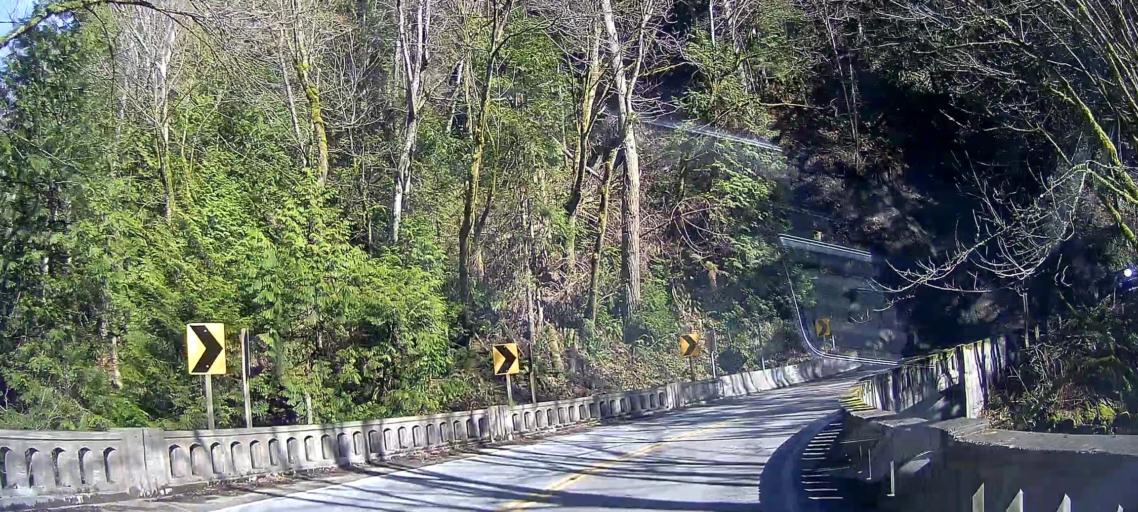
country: US
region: Washington
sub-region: Whatcom County
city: Geneva
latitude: 48.6180
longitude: -122.4396
